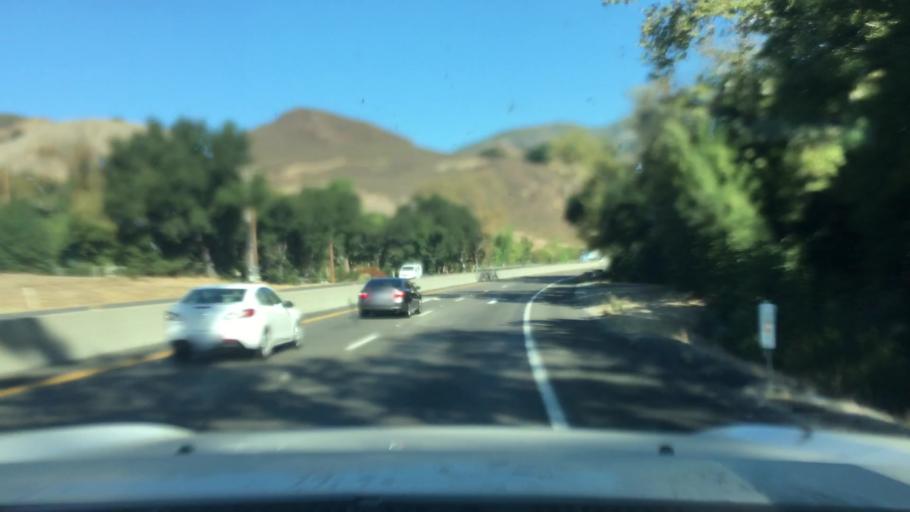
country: US
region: California
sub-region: San Luis Obispo County
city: San Luis Obispo
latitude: 35.3124
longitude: -120.6240
